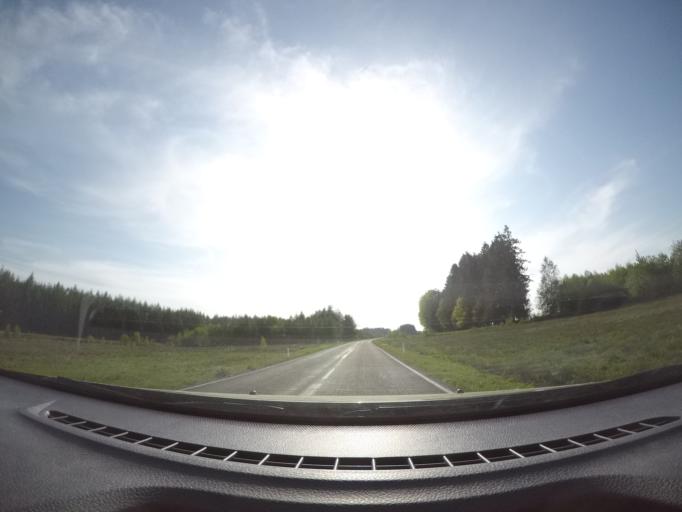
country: BE
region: Wallonia
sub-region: Province du Luxembourg
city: Tintigny
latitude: 49.6675
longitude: 5.5458
